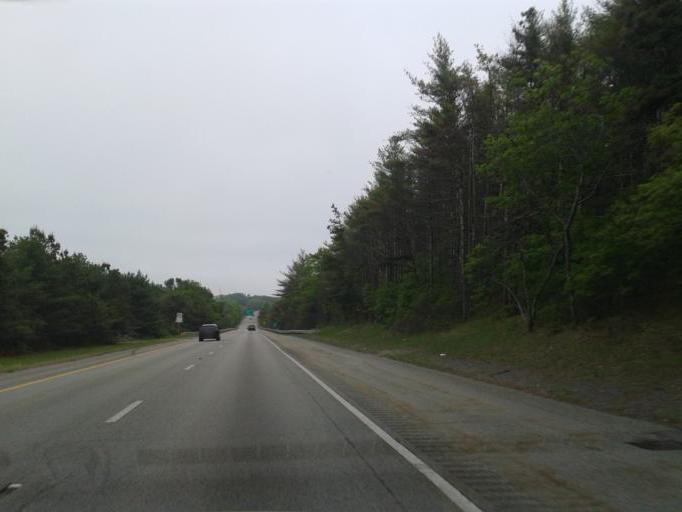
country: US
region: Massachusetts
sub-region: Barnstable County
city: Sagamore
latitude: 41.8329
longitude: -70.5647
